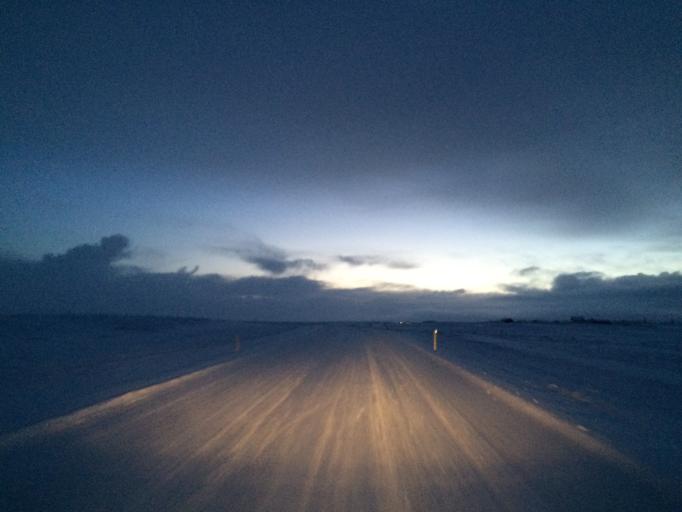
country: IS
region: South
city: Selfoss
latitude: 64.0919
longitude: -20.7325
